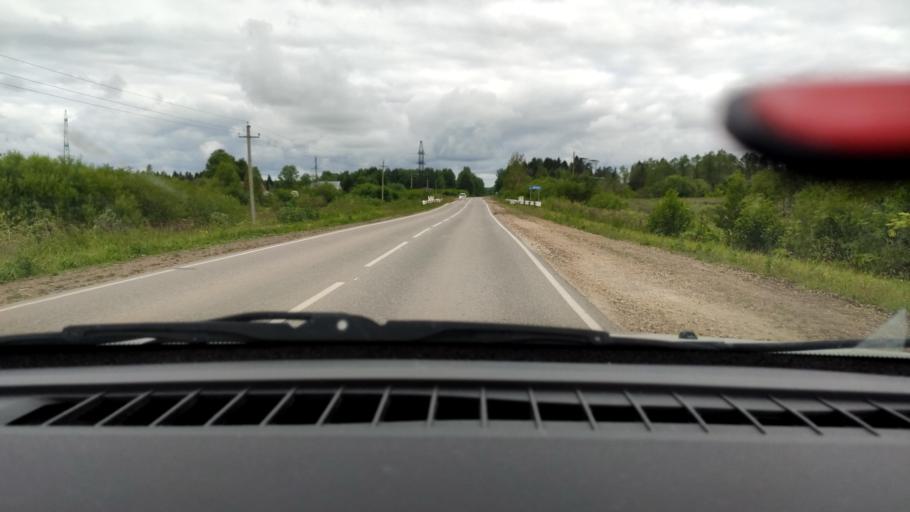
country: RU
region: Perm
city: Chaykovskaya
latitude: 58.0814
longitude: 55.6163
